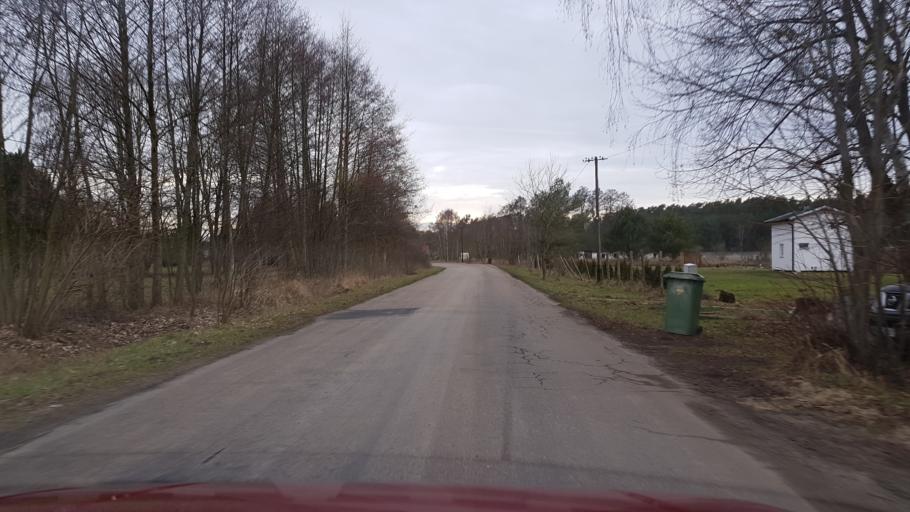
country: PL
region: West Pomeranian Voivodeship
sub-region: Powiat policki
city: Police
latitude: 53.5574
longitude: 14.4811
